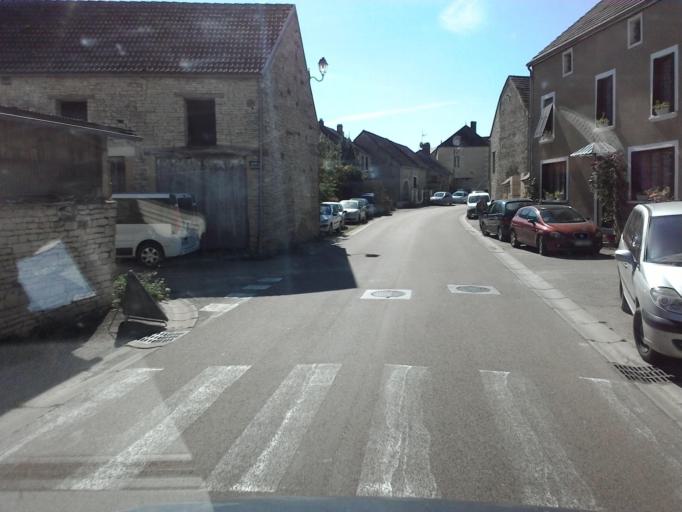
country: FR
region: Bourgogne
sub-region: Departement de l'Yonne
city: Joux-la-Ville
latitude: 47.6240
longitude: 3.8626
